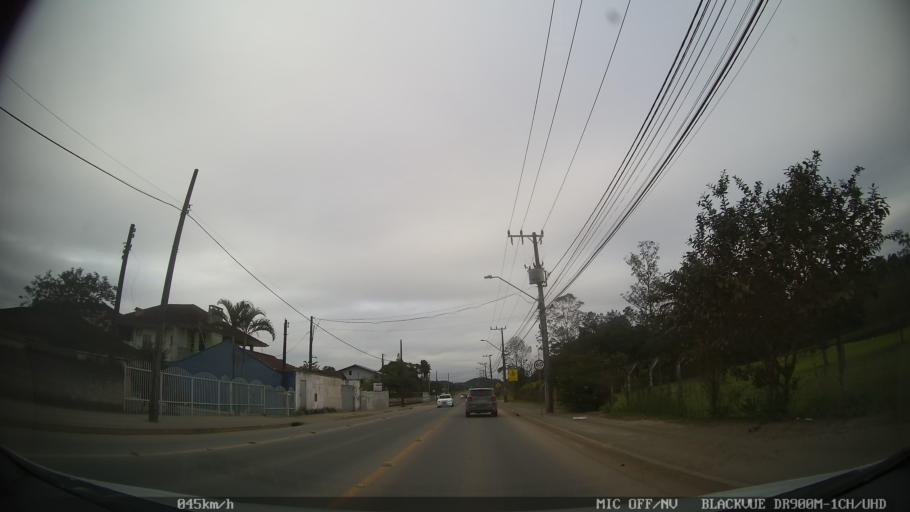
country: BR
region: Santa Catarina
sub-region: Joinville
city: Joinville
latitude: -26.3374
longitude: -48.8962
